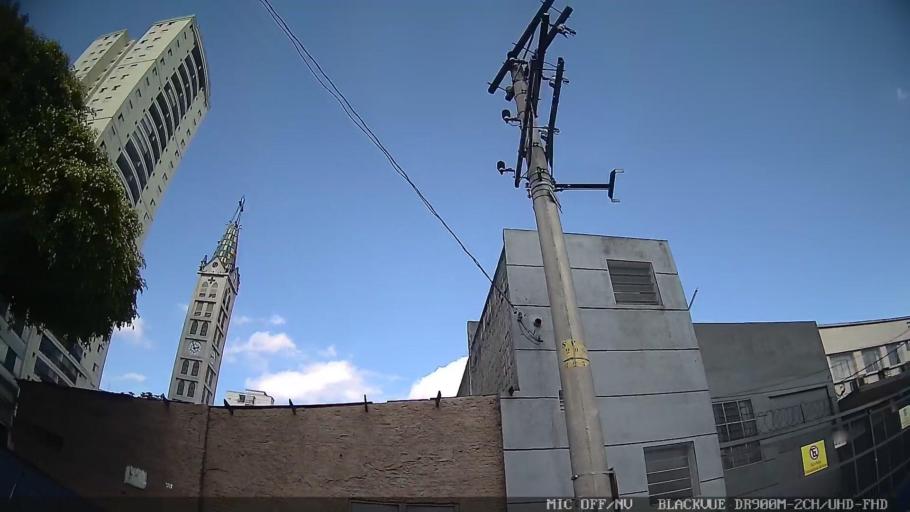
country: BR
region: Sao Paulo
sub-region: Sao Caetano Do Sul
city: Sao Caetano do Sul
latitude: -23.5939
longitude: -46.5998
